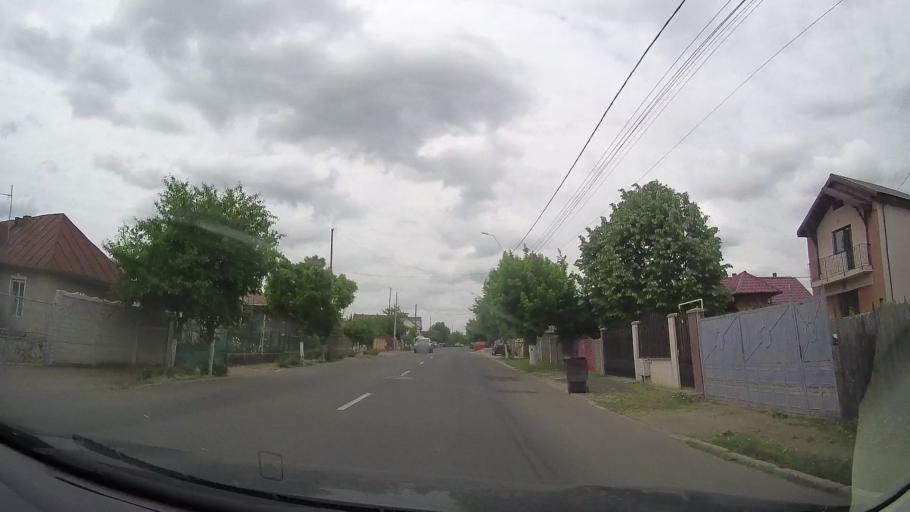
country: RO
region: Olt
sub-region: Municipiul Caracal
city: Caracal
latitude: 44.1126
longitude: 24.3337
